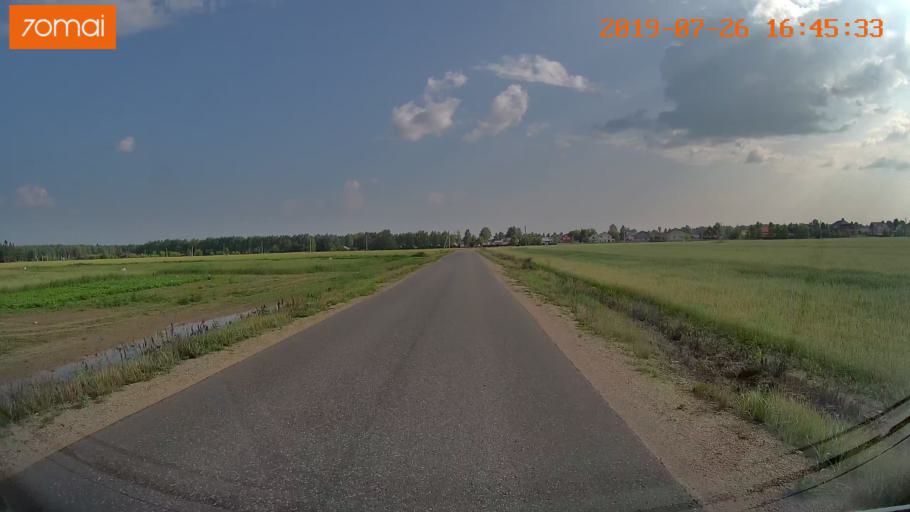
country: RU
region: Ivanovo
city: Bogorodskoye
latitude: 57.0488
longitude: 41.0220
